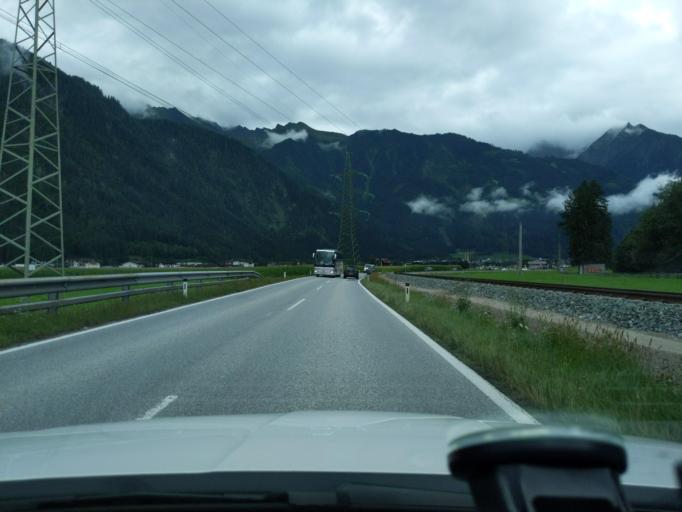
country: AT
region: Tyrol
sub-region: Politischer Bezirk Schwaz
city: Mayrhofen
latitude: 47.1827
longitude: 11.8667
